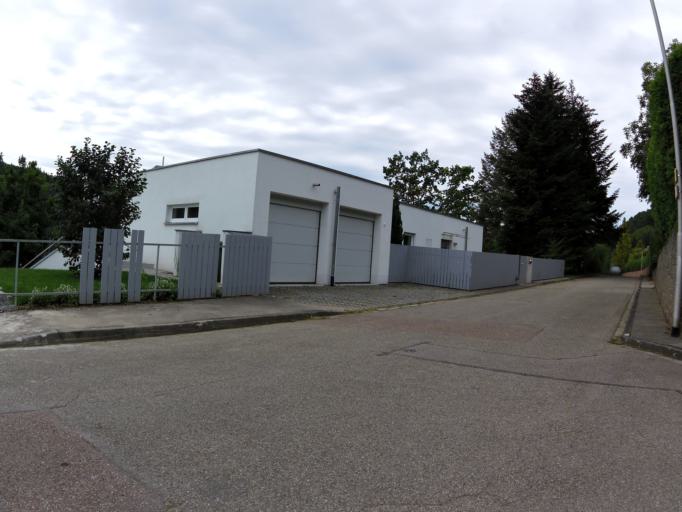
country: DE
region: Baden-Wuerttemberg
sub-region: Freiburg Region
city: Hohberg
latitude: 48.3409
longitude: 7.9066
